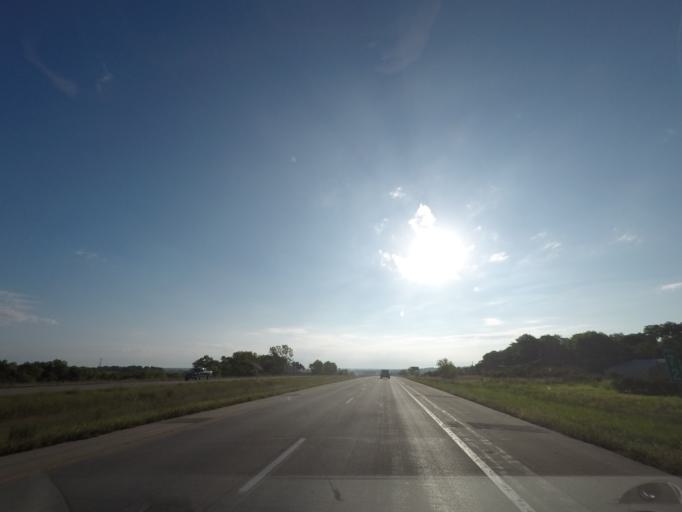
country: US
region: Iowa
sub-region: Warren County
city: Carlisle
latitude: 41.5117
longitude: -93.5437
